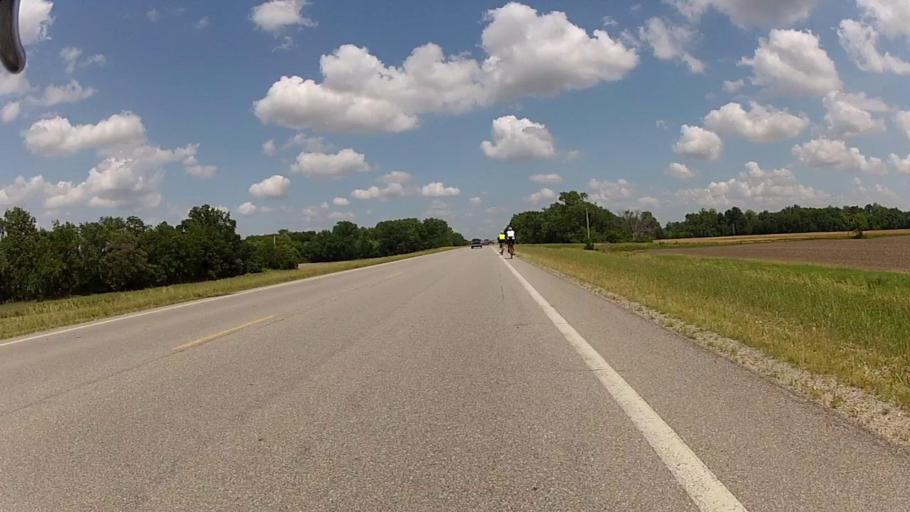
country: US
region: Kansas
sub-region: Labette County
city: Oswego
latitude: 37.1938
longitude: -95.1961
